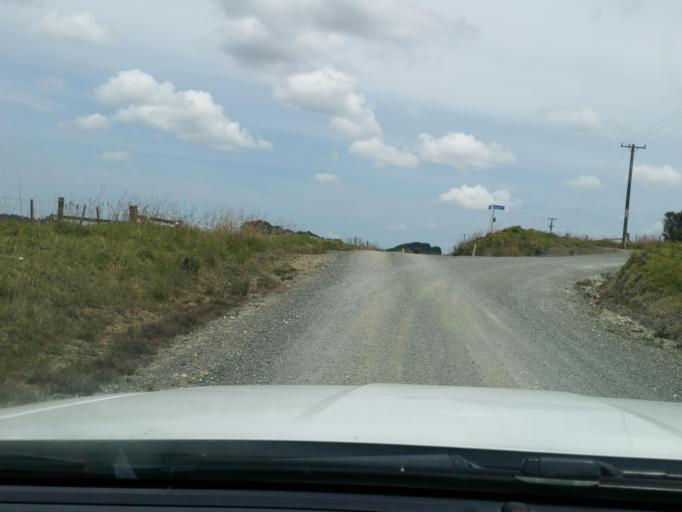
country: NZ
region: Northland
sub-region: Whangarei
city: Ruakaka
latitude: -35.9801
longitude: 174.2330
